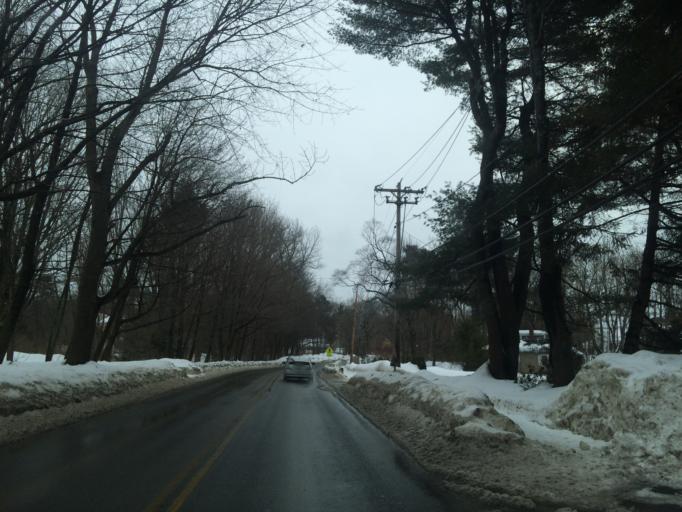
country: US
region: Massachusetts
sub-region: Middlesex County
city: Lincoln
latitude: 42.4115
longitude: -71.3352
